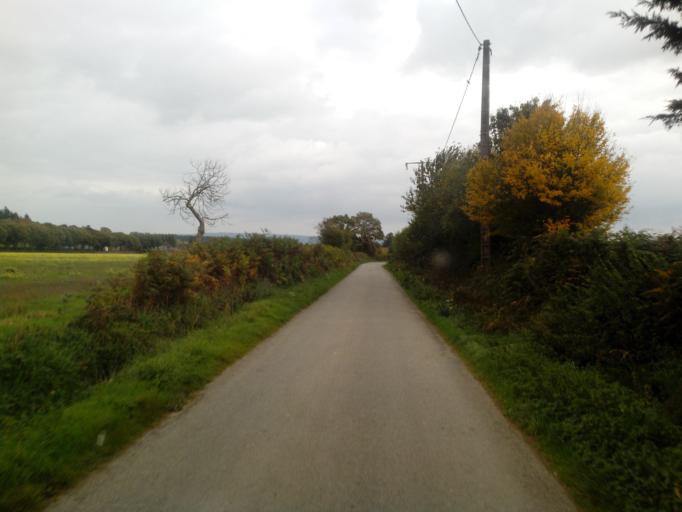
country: FR
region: Brittany
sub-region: Departement du Morbihan
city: Guilliers
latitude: 48.0923
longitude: -2.3708
